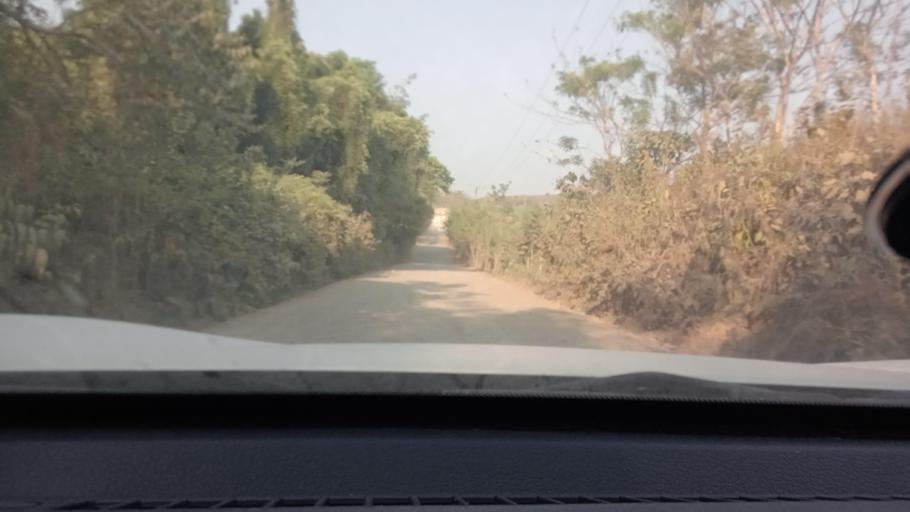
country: MX
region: Tabasco
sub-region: Huimanguillo
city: Francisco Rueda
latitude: 17.6575
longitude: -93.8664
